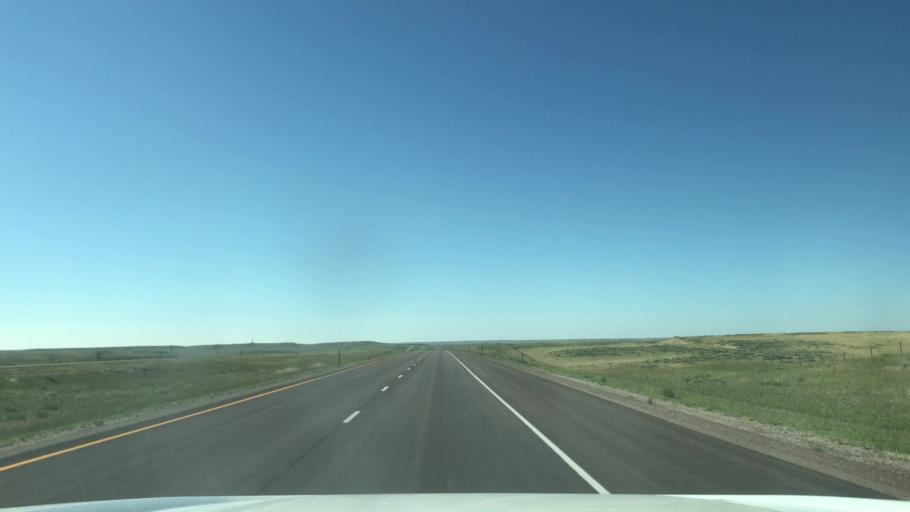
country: US
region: Wyoming
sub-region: Laramie County
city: Ranchettes
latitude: 41.5059
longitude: -104.8994
